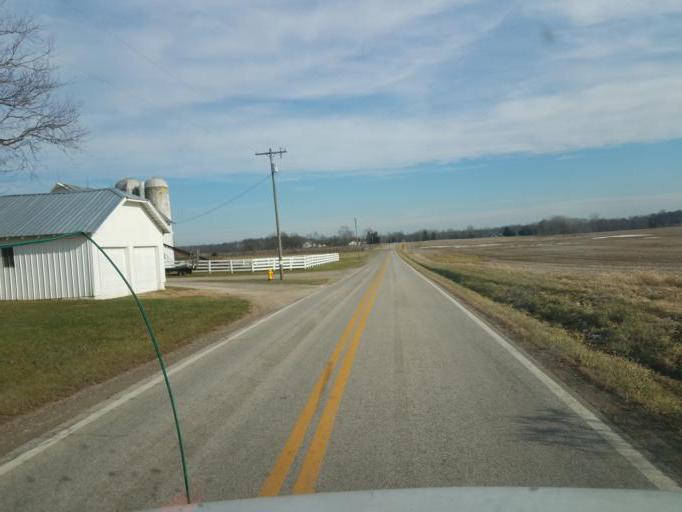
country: US
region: Ohio
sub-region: Delaware County
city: Ashley
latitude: 40.3563
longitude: -82.9756
